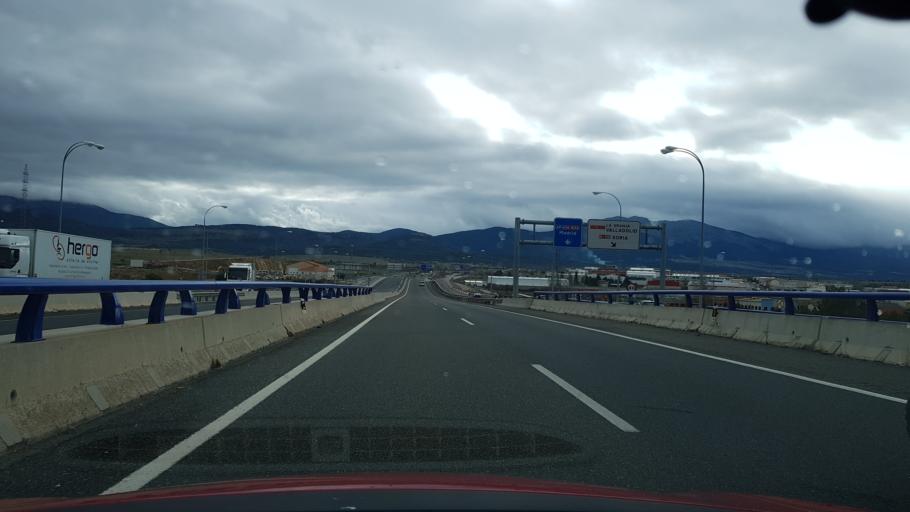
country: ES
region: Castille and Leon
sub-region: Provincia de Segovia
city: Segovia
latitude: 40.9207
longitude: -4.1078
